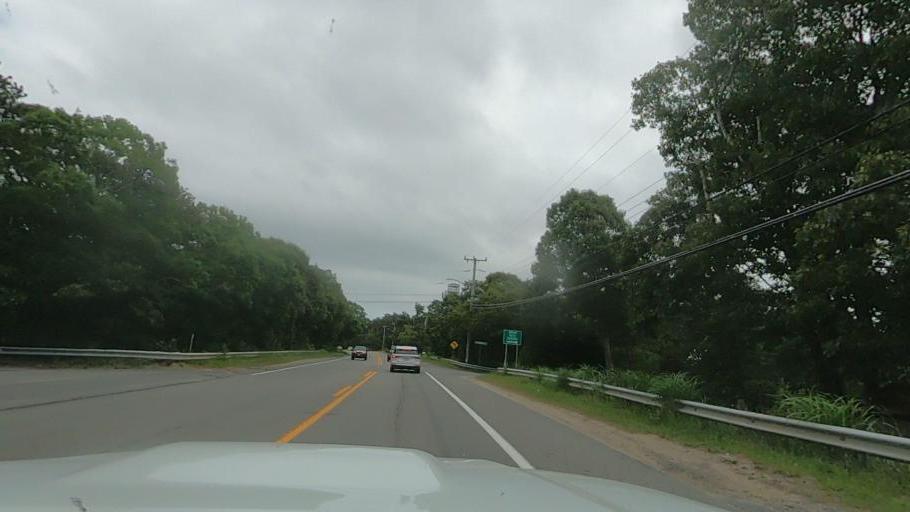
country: US
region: Massachusetts
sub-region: Barnstable County
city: Wellfleet
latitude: 41.9211
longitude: -70.0079
